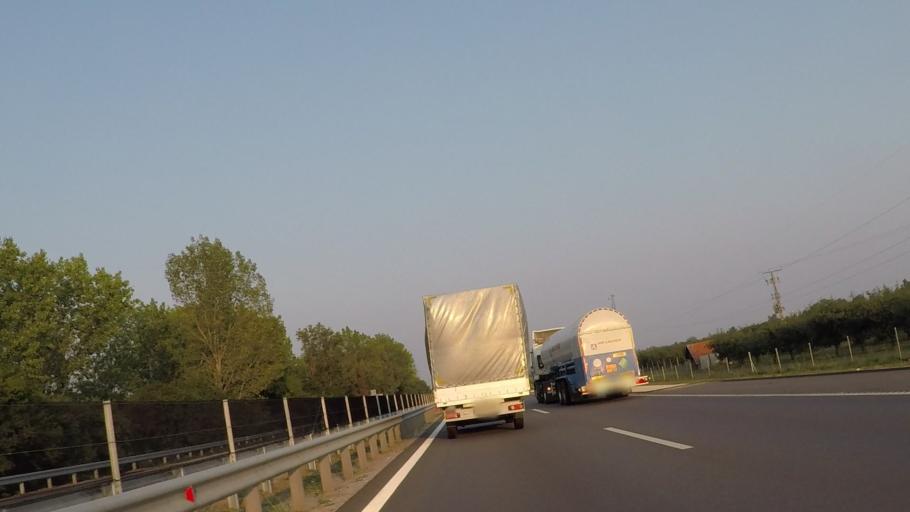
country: HU
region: Pest
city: Cegledbercel
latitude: 47.2184
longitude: 19.7068
